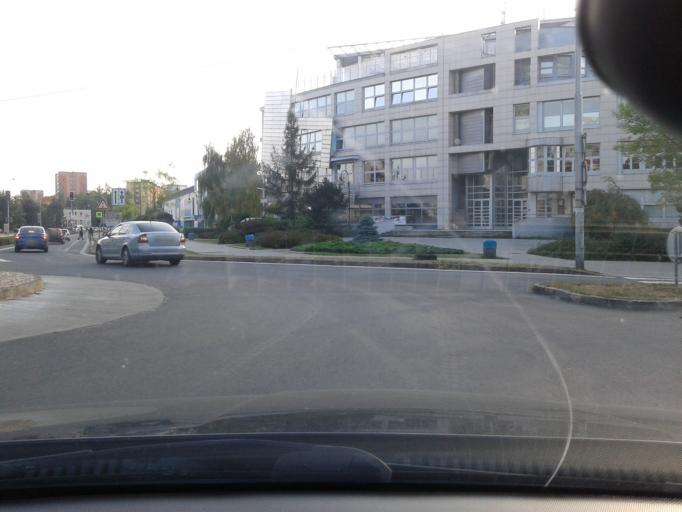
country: CZ
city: Dolni Lutyne
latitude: 49.8727
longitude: 18.4262
